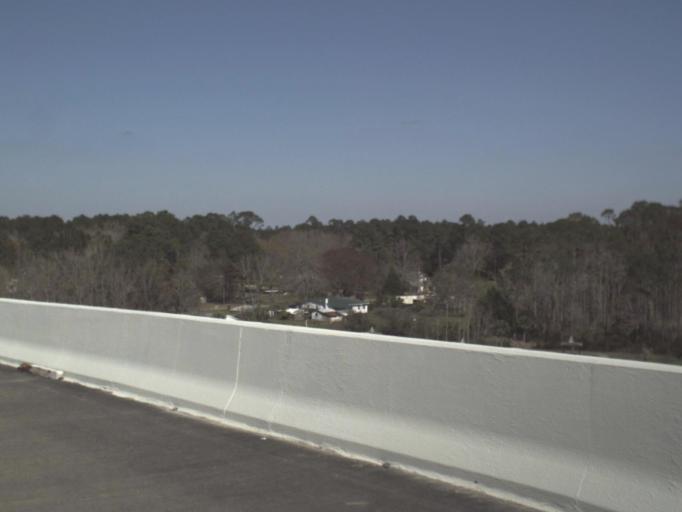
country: US
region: Florida
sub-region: Gulf County
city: Port Saint Joe
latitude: 29.8803
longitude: -85.2222
